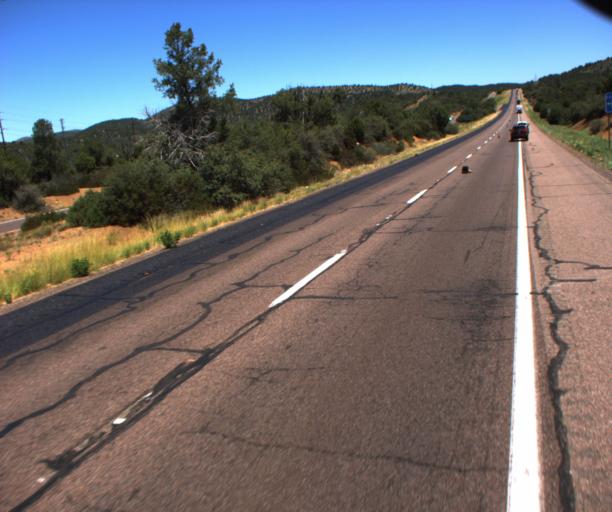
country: US
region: Arizona
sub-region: Gila County
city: Payson
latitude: 34.1788
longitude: -111.3366
